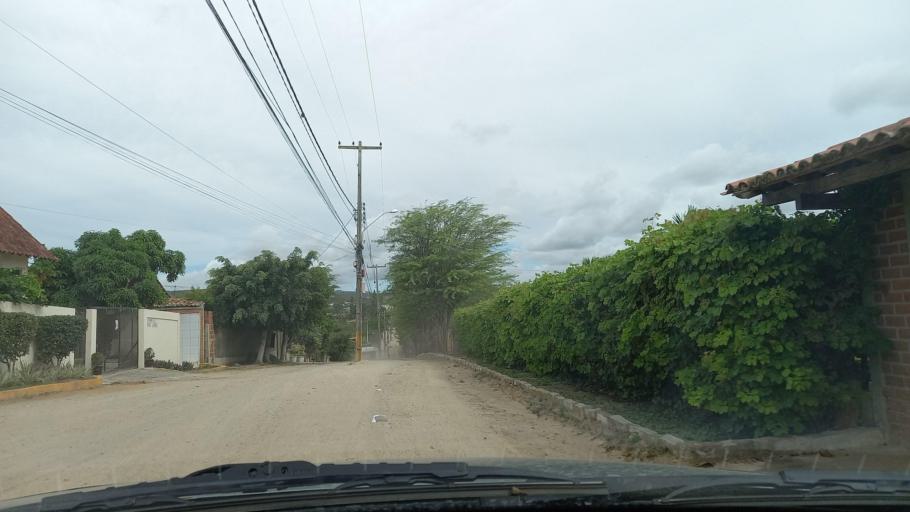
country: BR
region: Pernambuco
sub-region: Gravata
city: Gravata
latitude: -8.1950
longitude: -35.6002
